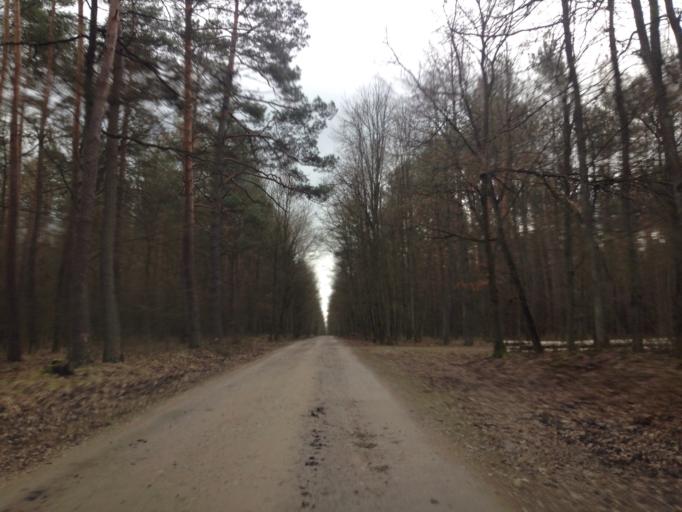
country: PL
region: Kujawsko-Pomorskie
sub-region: Powiat brodnicki
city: Gorzno
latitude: 53.2042
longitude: 19.6916
